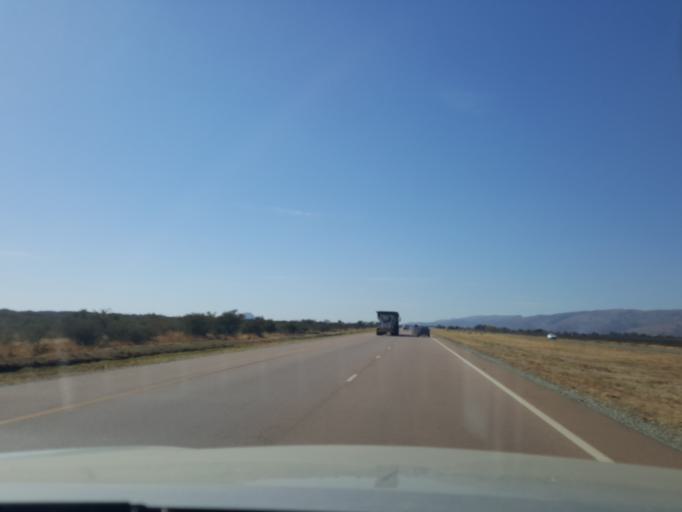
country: ZA
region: North-West
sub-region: Bojanala Platinum District Municipality
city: Brits
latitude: -25.7369
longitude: 27.6200
